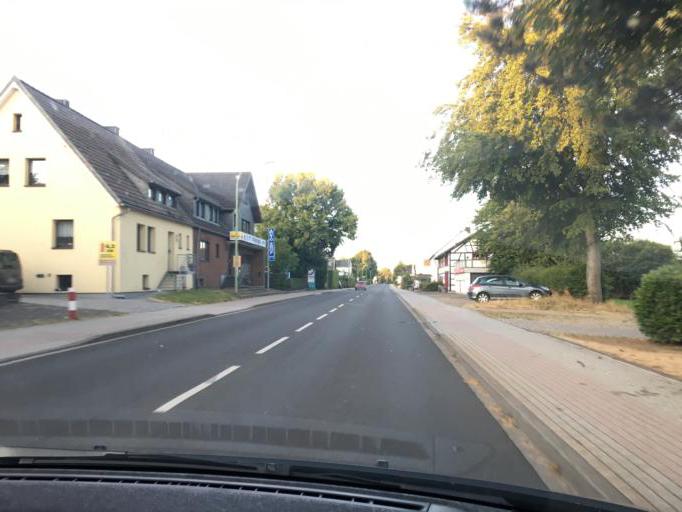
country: DE
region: North Rhine-Westphalia
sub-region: Regierungsbezirk Koln
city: Simmerath
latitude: 50.6053
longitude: 6.2995
